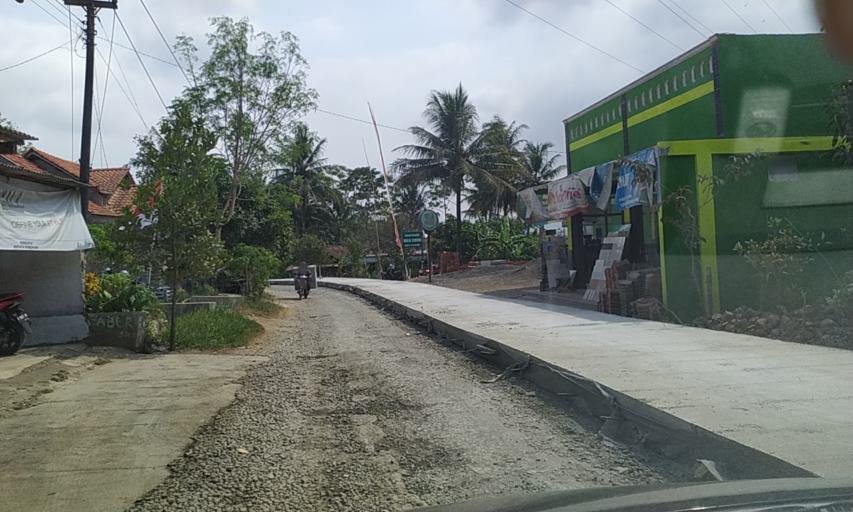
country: ID
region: Central Java
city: Madusari
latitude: -7.6437
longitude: 109.0763
